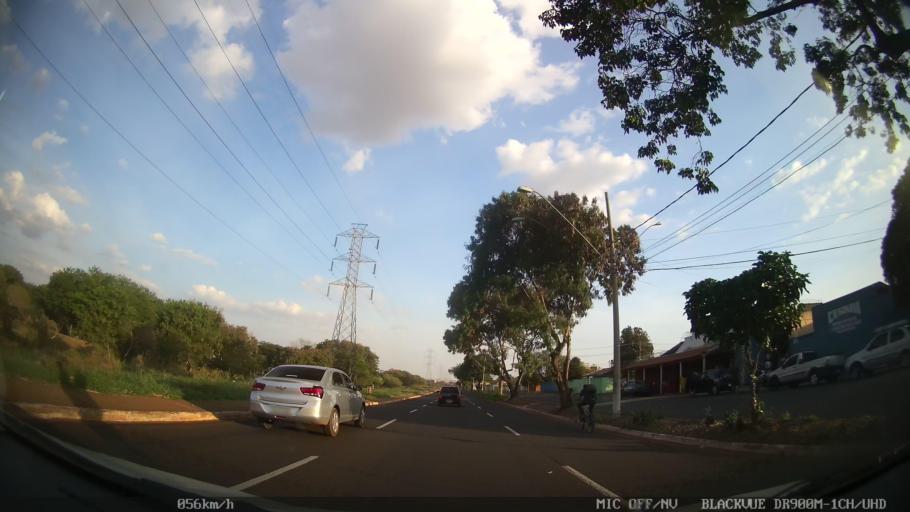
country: BR
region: Sao Paulo
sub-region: Ribeirao Preto
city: Ribeirao Preto
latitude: -21.1247
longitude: -47.8033
